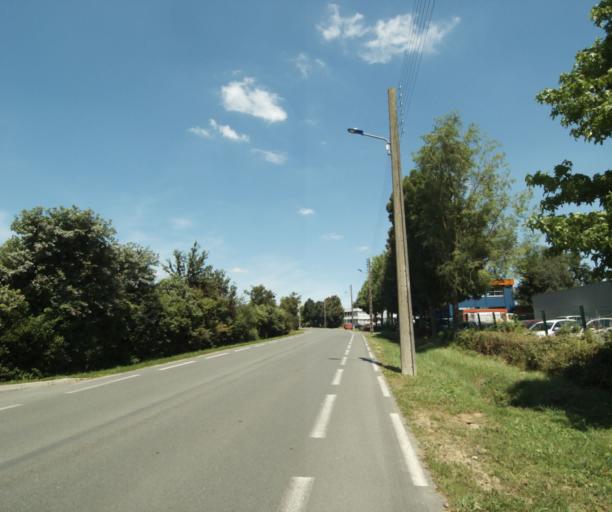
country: FR
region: Pays de la Loire
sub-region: Departement de la Mayenne
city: Laval
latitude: 48.0799
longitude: -0.7490
